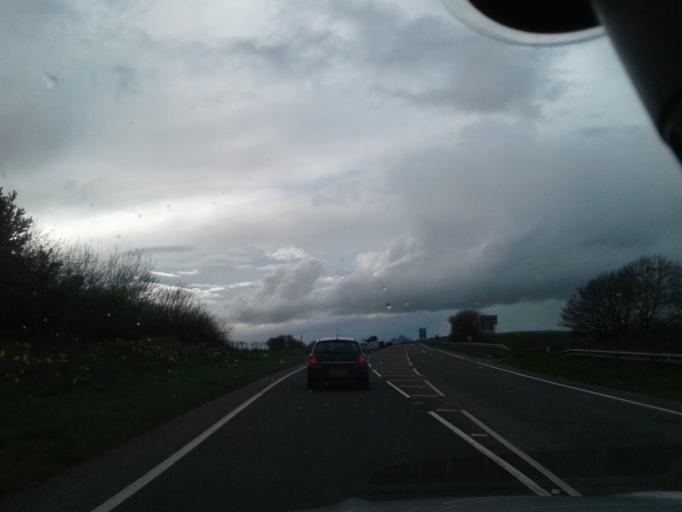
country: GB
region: Northern Ireland
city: Newtownstewart
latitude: 54.7229
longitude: -7.3934
